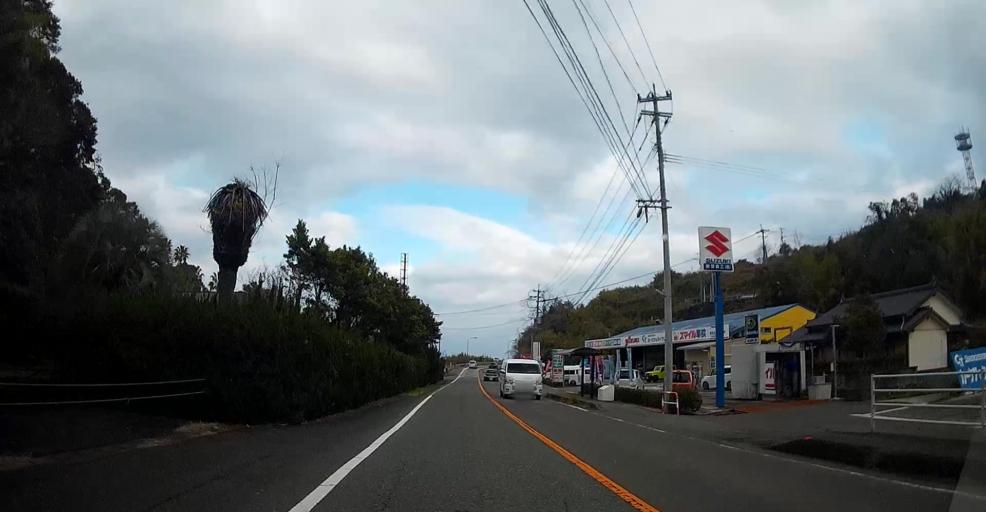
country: JP
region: Kumamoto
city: Hondo
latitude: 32.4995
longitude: 130.2986
